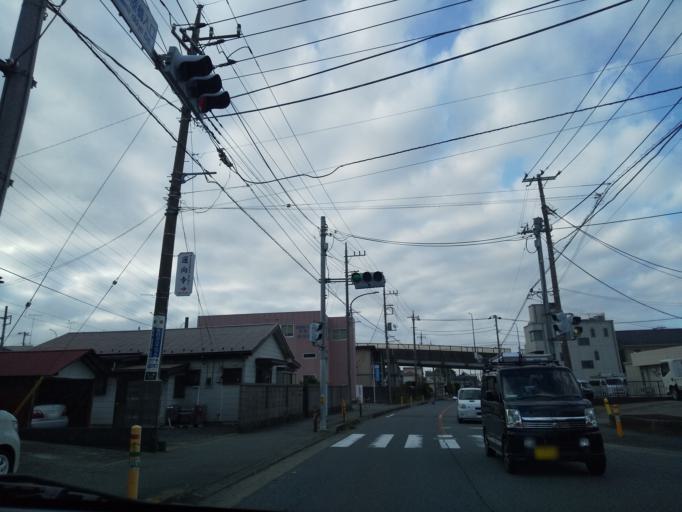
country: JP
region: Kanagawa
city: Zama
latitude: 35.5339
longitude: 139.3717
